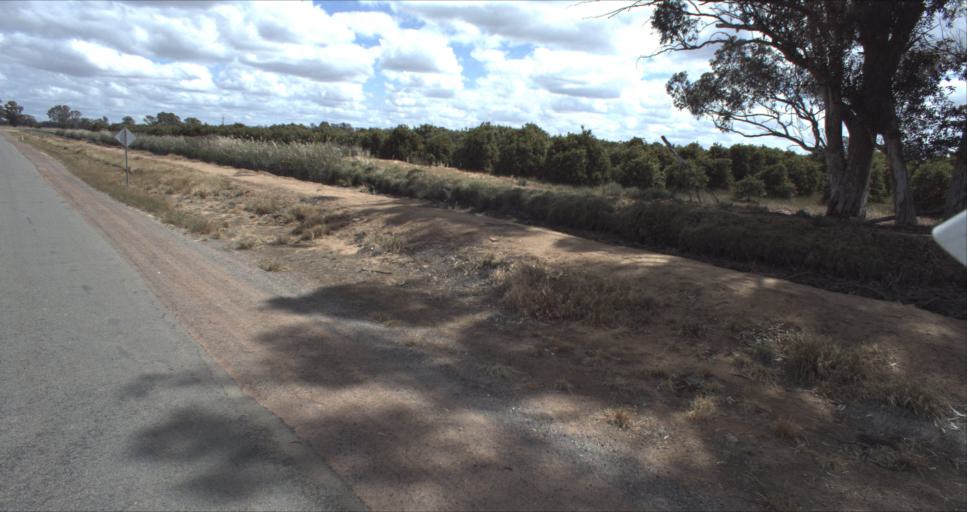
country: AU
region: New South Wales
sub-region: Leeton
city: Leeton
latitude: -34.5878
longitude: 146.3712
